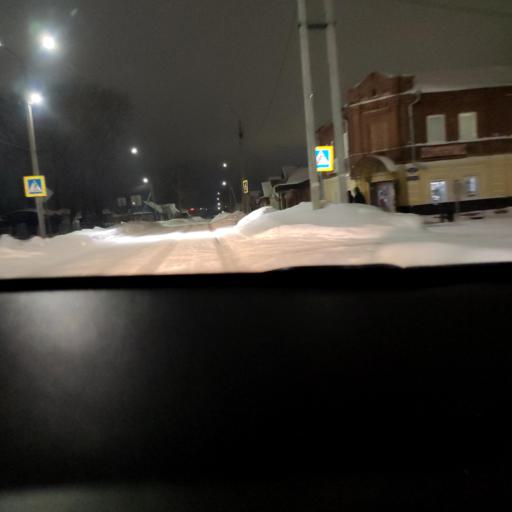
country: RU
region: Tatarstan
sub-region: Chistopol'skiy Rayon
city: Chistopol'
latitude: 55.3647
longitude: 50.6291
